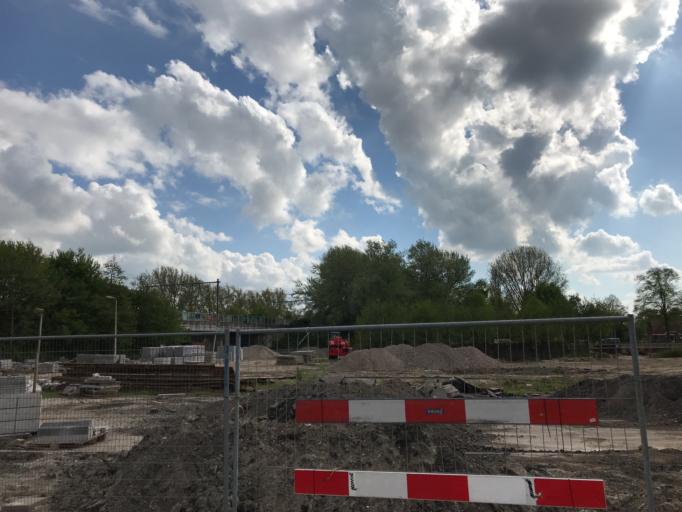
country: NL
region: North Holland
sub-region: Gemeente Diemen
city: Diemen
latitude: 52.3369
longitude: 4.9673
